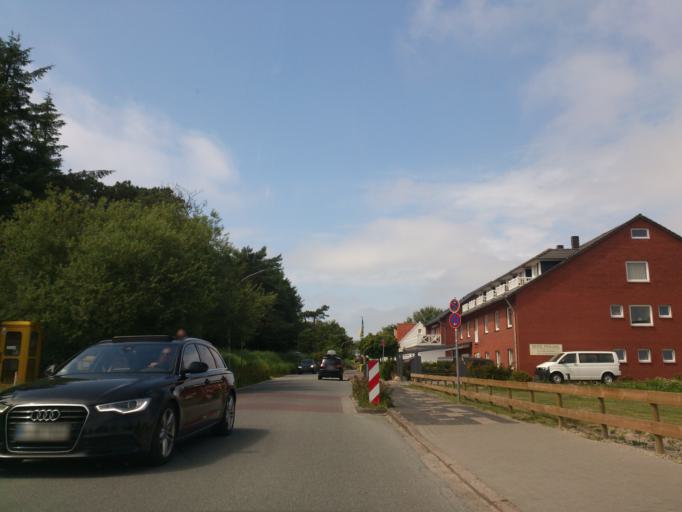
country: DE
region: Schleswig-Holstein
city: Sankt Peter-Ording
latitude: 54.3231
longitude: 8.6103
